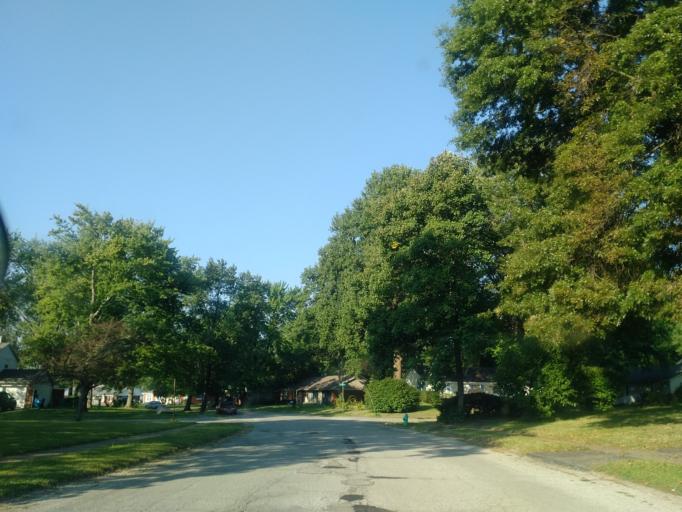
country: US
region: Indiana
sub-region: Marion County
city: Cumberland
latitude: 39.7955
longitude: -85.9875
